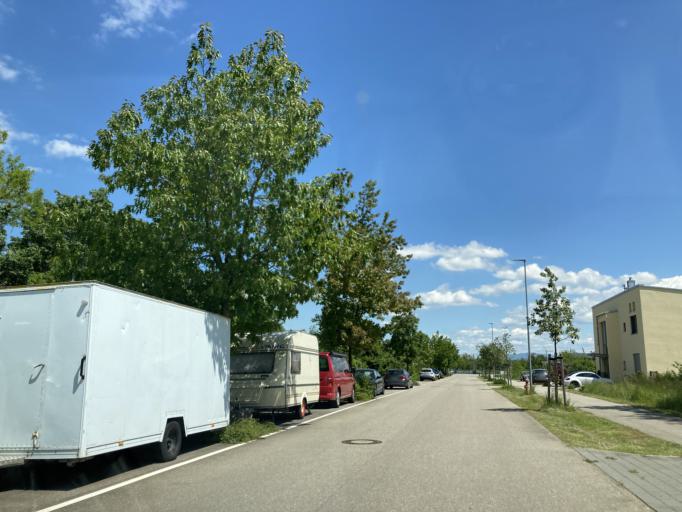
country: DE
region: Baden-Wuerttemberg
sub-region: Freiburg Region
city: Eschbach
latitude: 47.8973
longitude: 7.6202
